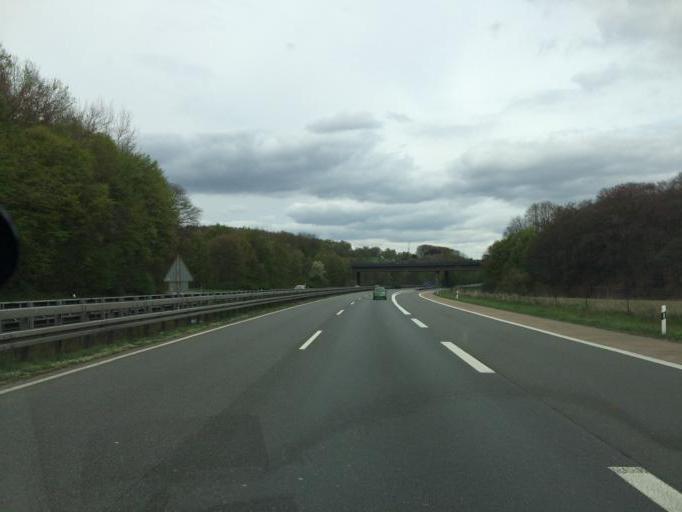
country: DE
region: North Rhine-Westphalia
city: Sprockhovel
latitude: 51.3538
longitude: 7.2742
